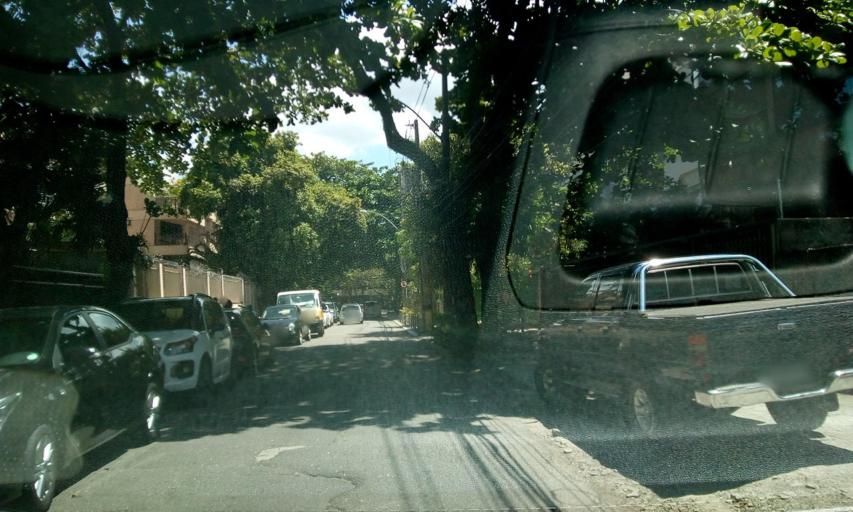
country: BR
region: Rio de Janeiro
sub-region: Rio De Janeiro
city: Rio de Janeiro
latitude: -23.0088
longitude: -43.3158
